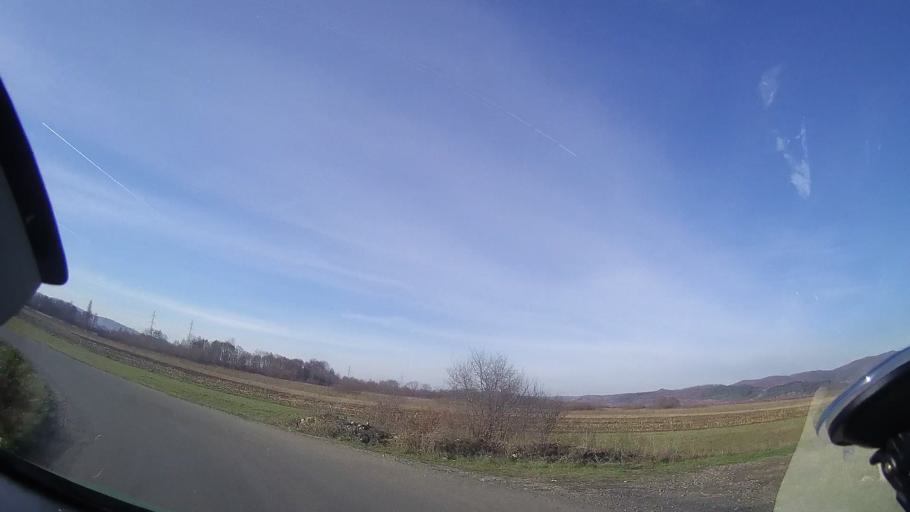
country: RO
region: Bihor
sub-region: Comuna Auseu
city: Grosi
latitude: 47.0286
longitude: 22.4832
